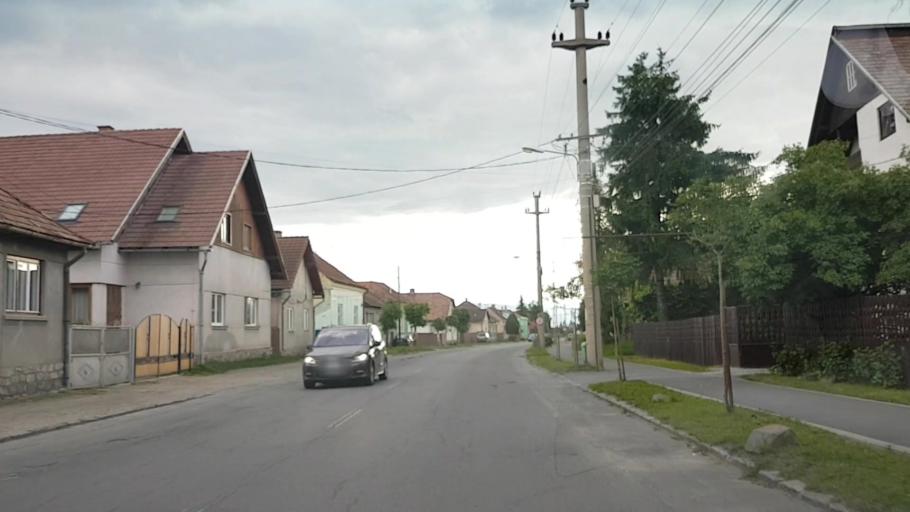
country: RO
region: Harghita
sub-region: Municipiul Gheorgheni
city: Gheorgheni
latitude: 46.7172
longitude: 25.5863
